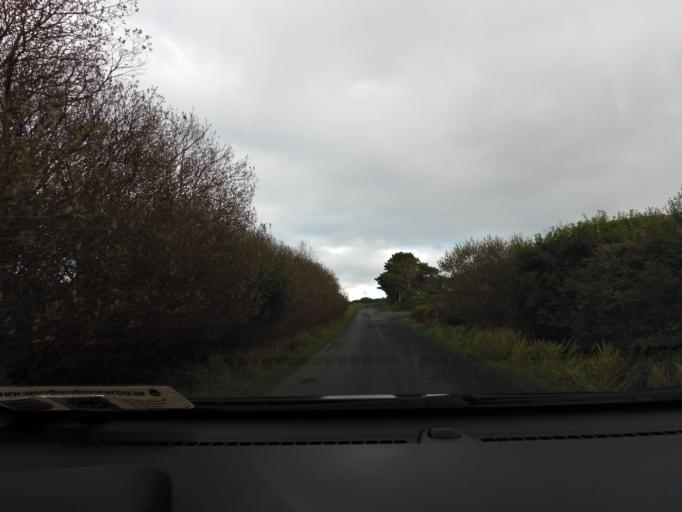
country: IE
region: Connaught
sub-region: Maigh Eo
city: Belmullet
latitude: 53.9275
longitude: -10.0174
